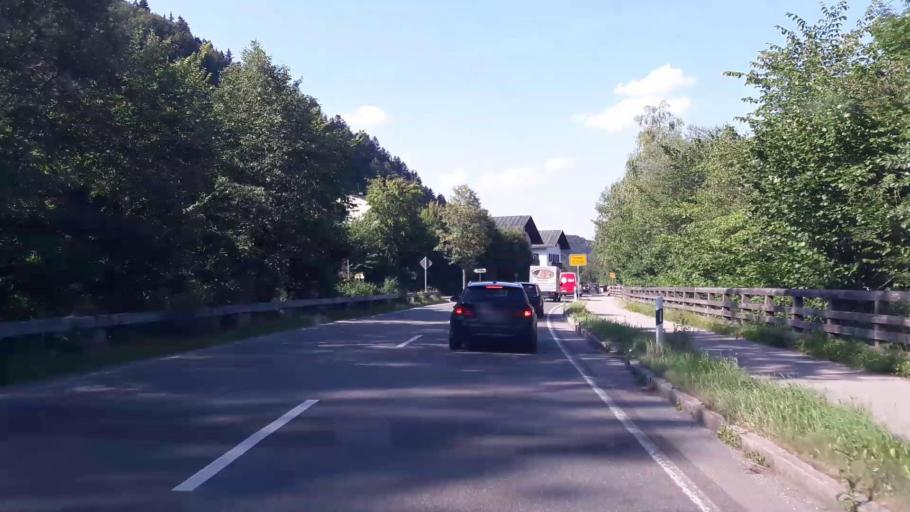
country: DE
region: Bavaria
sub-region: Upper Bavaria
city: Ruhpolding
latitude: 47.7927
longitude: 12.6368
